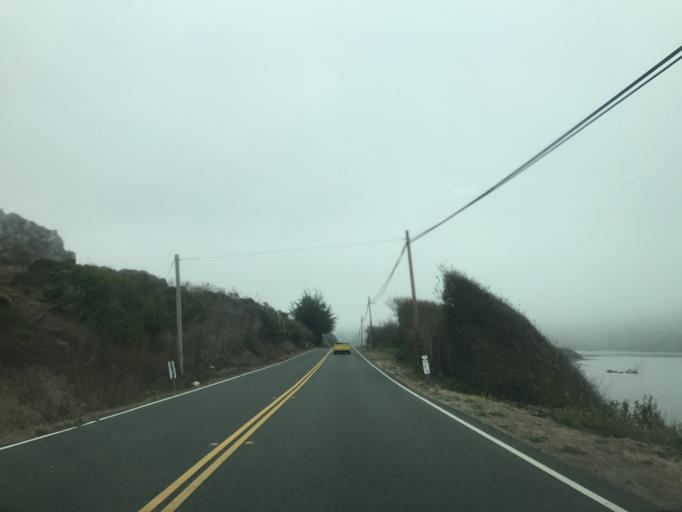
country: US
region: California
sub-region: Sonoma County
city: Monte Rio
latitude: 38.4447
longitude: -123.1111
